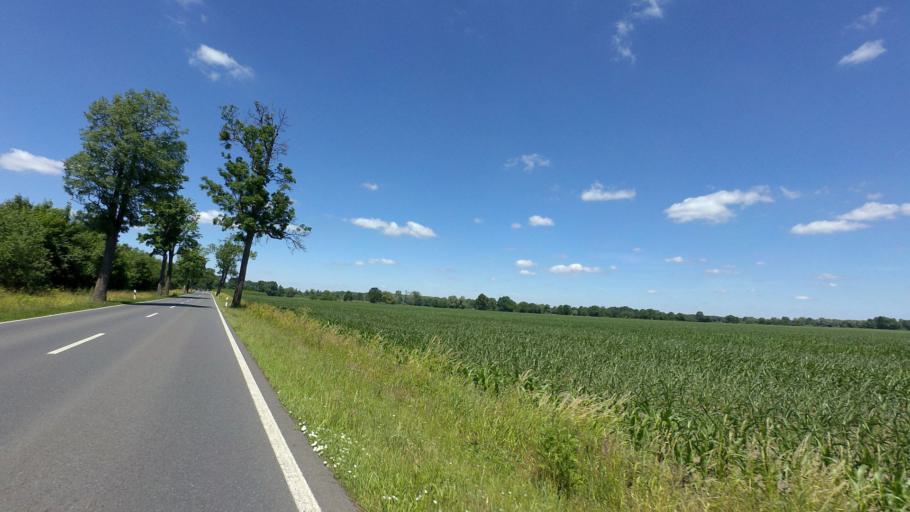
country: DE
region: Brandenburg
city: Golssen
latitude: 51.9579
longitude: 13.6298
